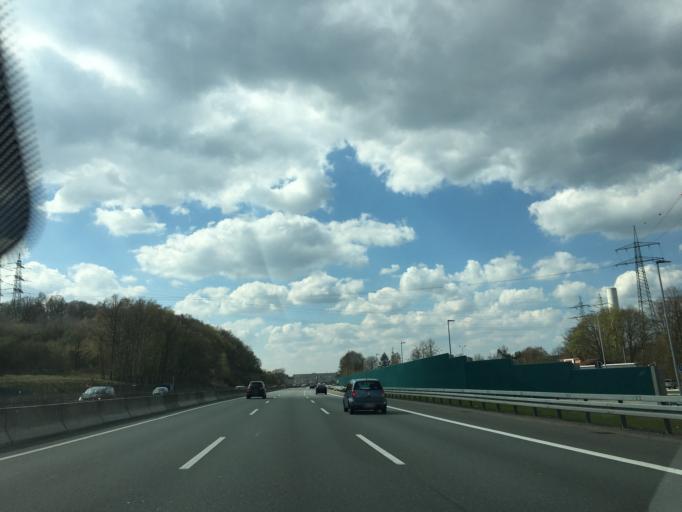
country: DE
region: North Rhine-Westphalia
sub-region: Regierungsbezirk Arnsberg
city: Hagen
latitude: 51.4120
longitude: 7.5016
